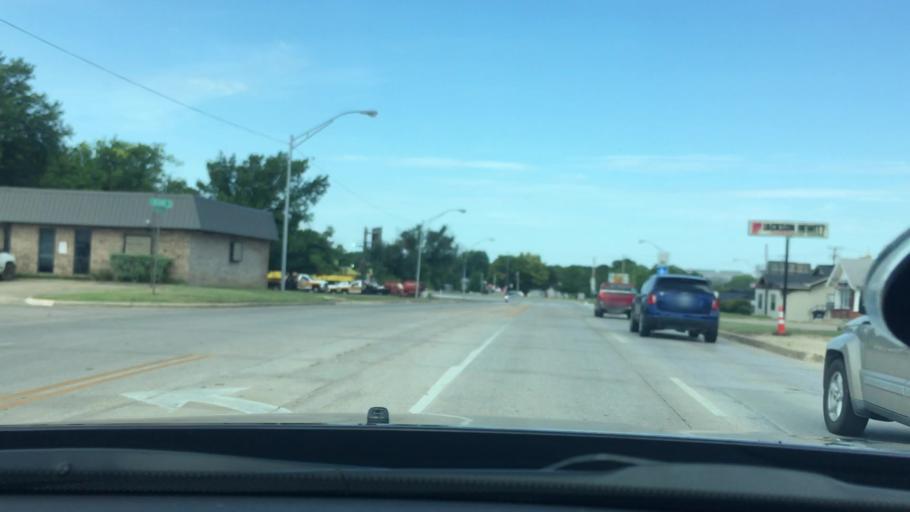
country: US
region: Oklahoma
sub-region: Pontotoc County
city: Ada
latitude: 34.7817
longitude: -96.6675
